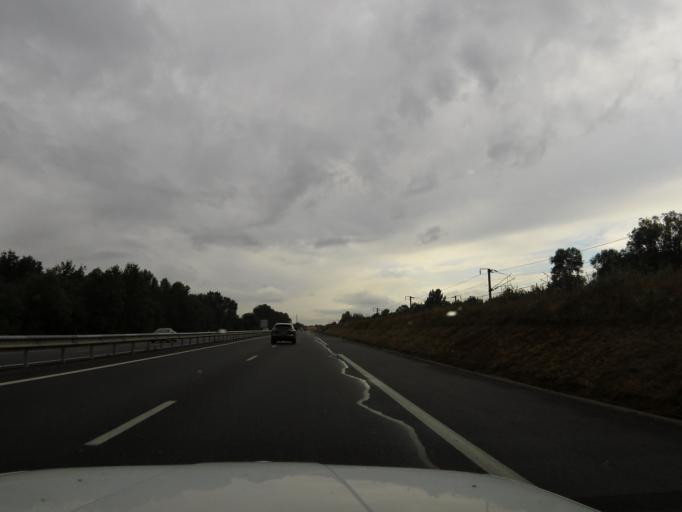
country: FR
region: Rhone-Alpes
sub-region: Departement du Rhone
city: Pusignan
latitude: 45.7789
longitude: 5.0819
